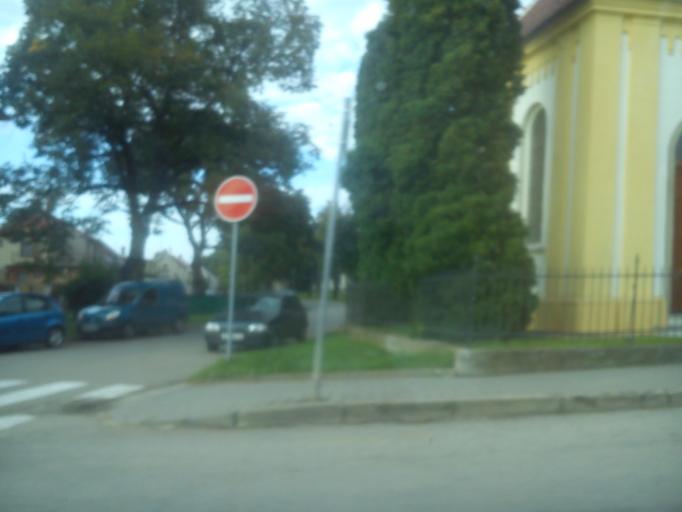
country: CZ
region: South Moravian
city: Sokolnice
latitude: 49.1141
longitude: 16.7214
